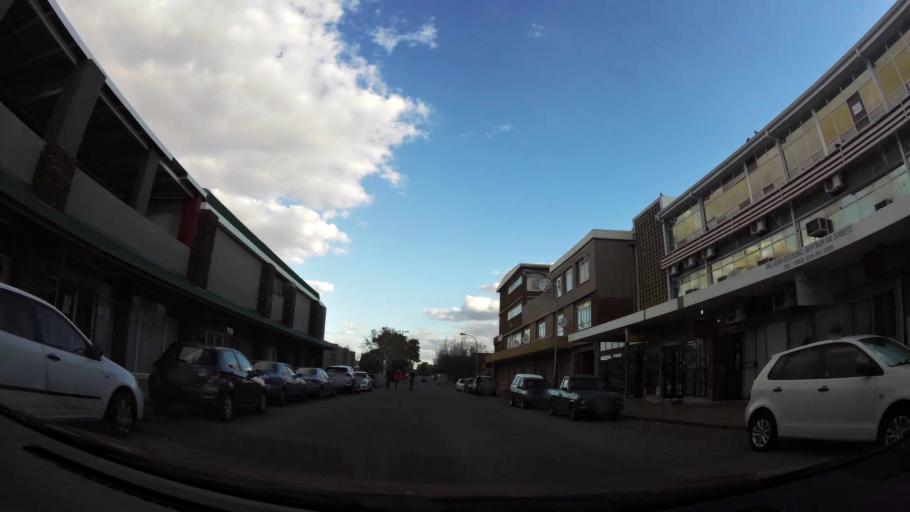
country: ZA
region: North-West
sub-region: Dr Kenneth Kaunda District Municipality
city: Potchefstroom
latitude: -26.7111
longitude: 27.0963
